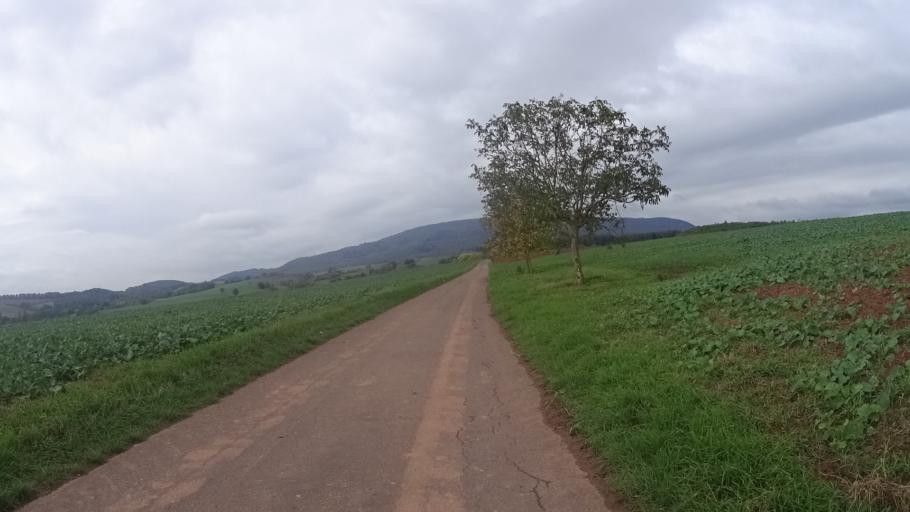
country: DE
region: Rheinland-Pfalz
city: Bennhausen
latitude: 49.6221
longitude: 7.9890
